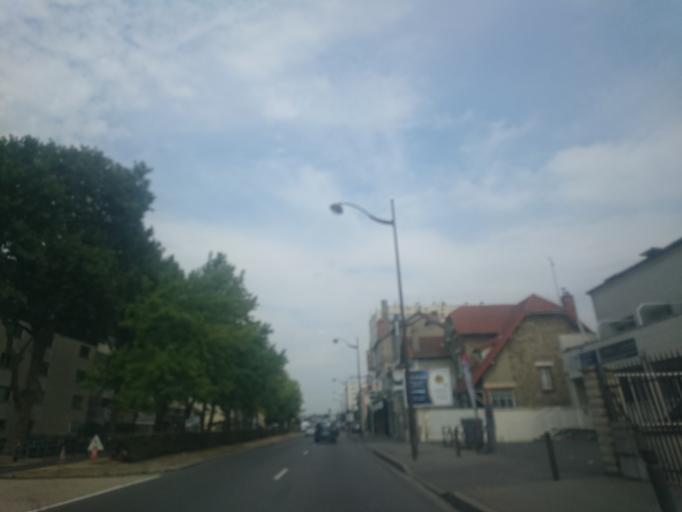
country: FR
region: Ile-de-France
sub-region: Departement de l'Essonne
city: Viry-Chatillon
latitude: 48.6746
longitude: 2.3871
